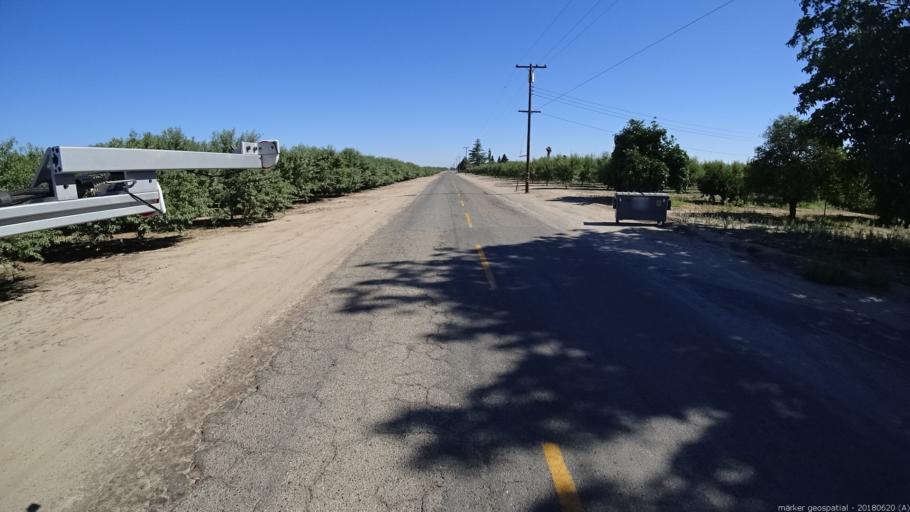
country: US
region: California
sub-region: Madera County
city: Parkwood
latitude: 36.8696
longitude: -120.0375
